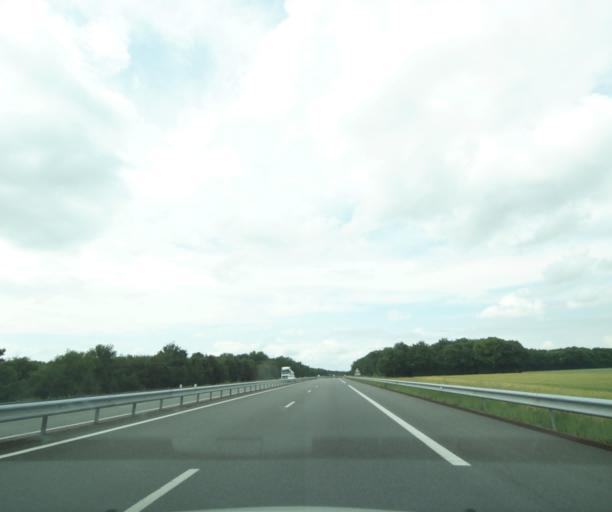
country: FR
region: Centre
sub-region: Departement du Cher
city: Levet
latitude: 46.8761
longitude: 2.4233
